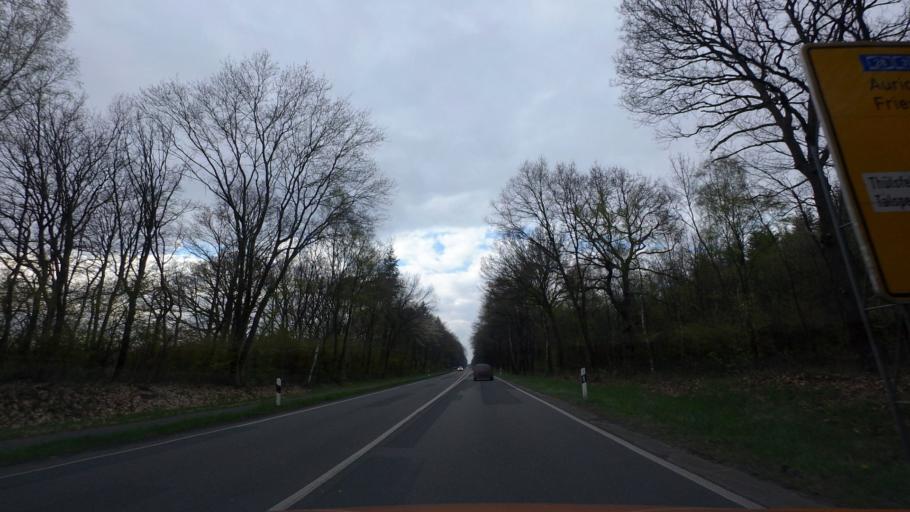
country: DE
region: Lower Saxony
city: Bosel
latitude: 52.9366
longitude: 7.9452
